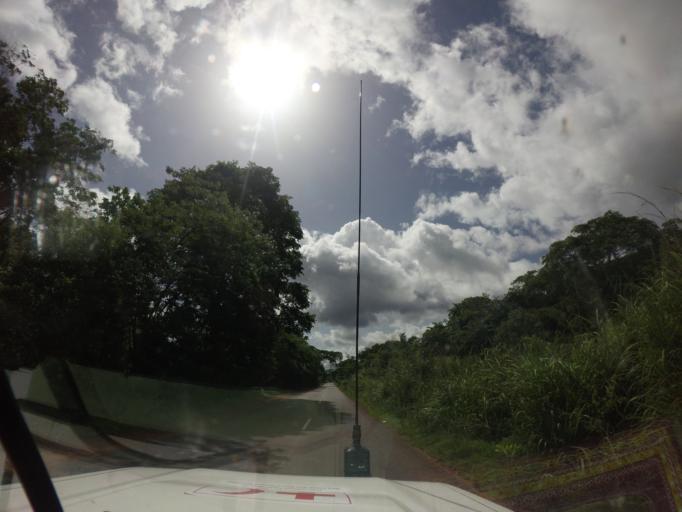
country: GN
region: Mamou
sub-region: Mamou Prefecture
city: Mamou
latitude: 10.3273
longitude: -12.0239
